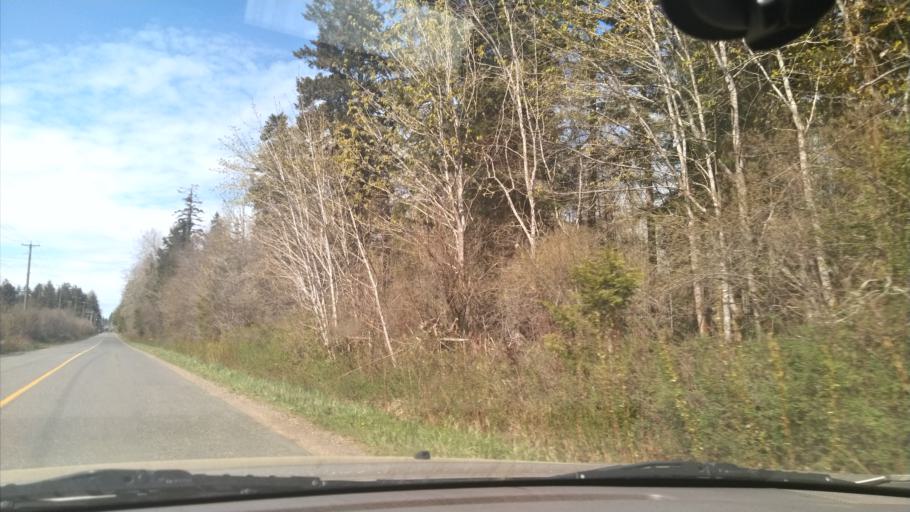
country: CA
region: British Columbia
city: Courtenay
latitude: 49.6976
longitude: -125.0141
